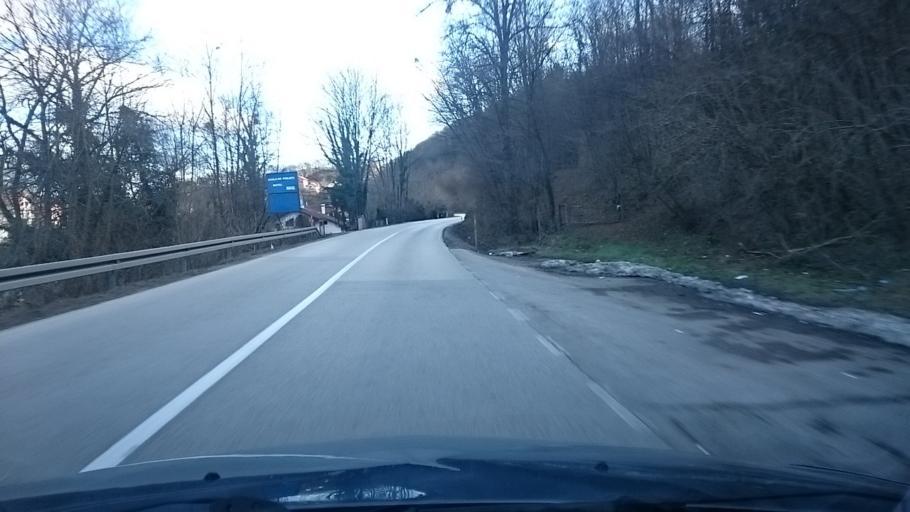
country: BA
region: Republika Srpska
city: Hiseti
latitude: 44.7002
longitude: 17.1854
